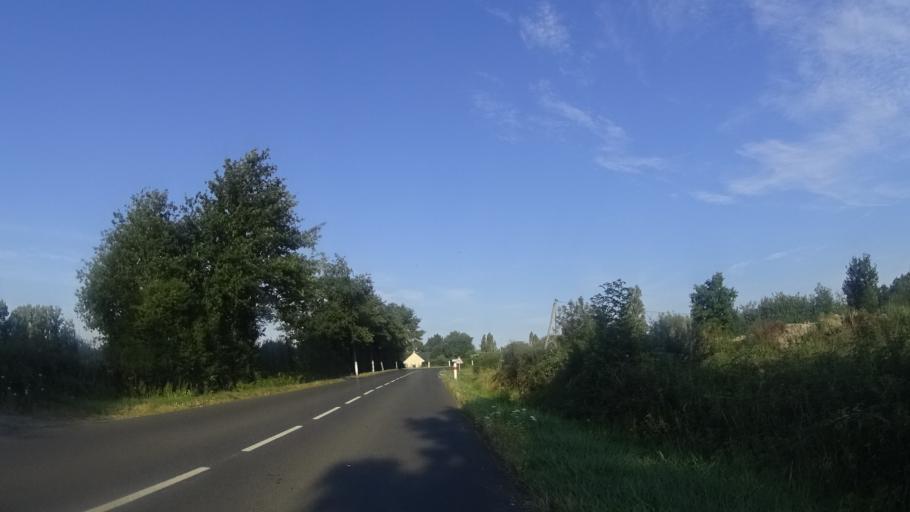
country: FR
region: Pays de la Loire
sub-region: Departement de la Loire-Atlantique
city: Riaille
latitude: 47.5145
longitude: -1.2817
